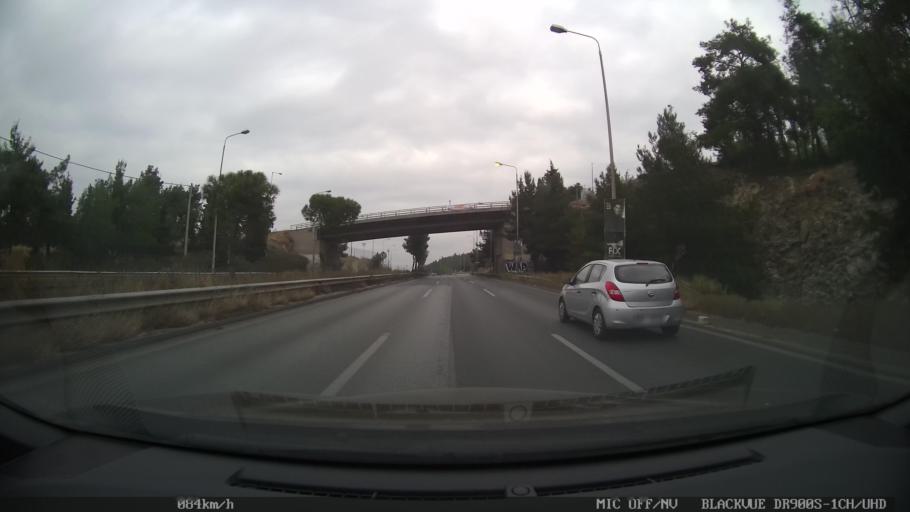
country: GR
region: Central Macedonia
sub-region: Nomos Thessalonikis
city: Agios Pavlos
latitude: 40.6422
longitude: 22.9697
